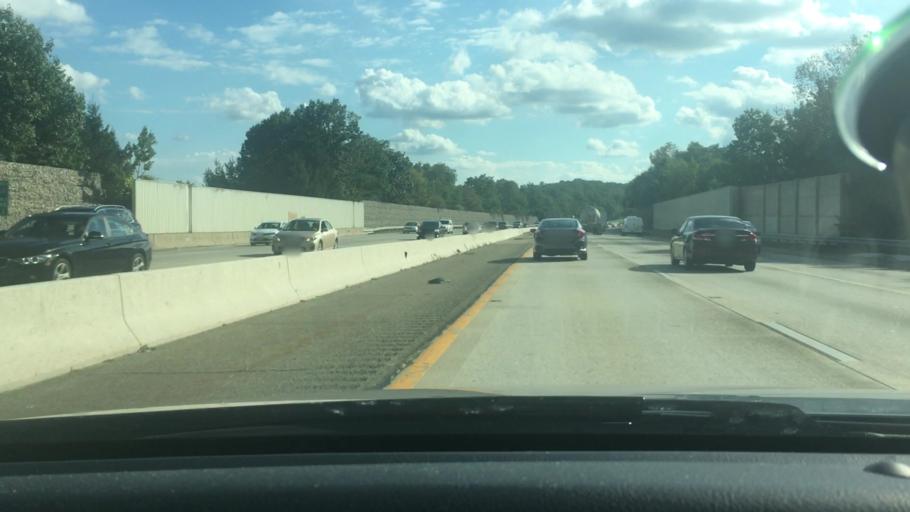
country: US
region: New Jersey
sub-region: Morris County
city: Boonton
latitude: 40.9286
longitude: -74.3584
